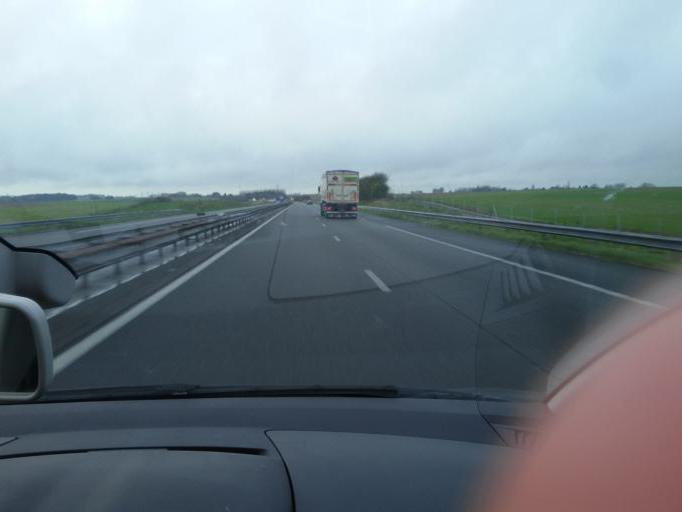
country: FR
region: Picardie
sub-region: Departement de la Somme
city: Moislains
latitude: 50.0604
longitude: 2.9620
